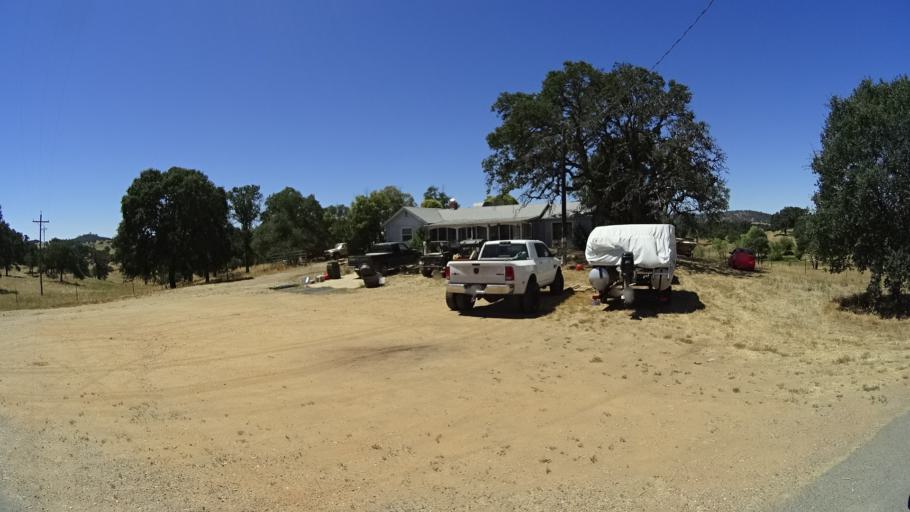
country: US
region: California
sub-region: Calaveras County
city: Copperopolis
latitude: 38.0350
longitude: -120.7225
